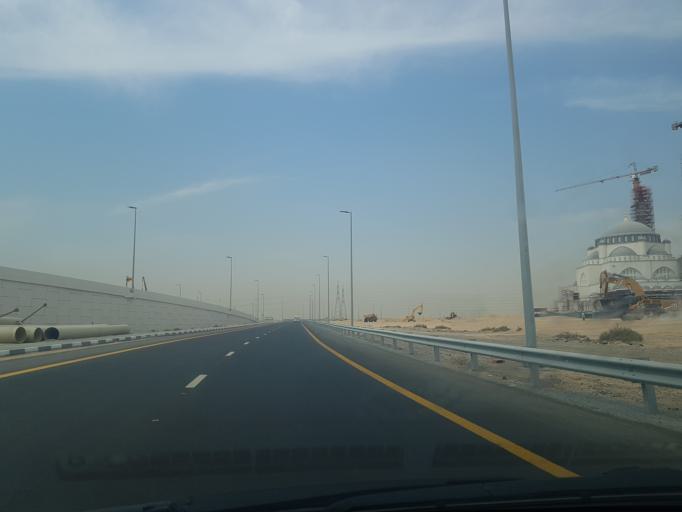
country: AE
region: Ash Shariqah
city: Sharjah
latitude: 25.2378
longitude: 55.5700
